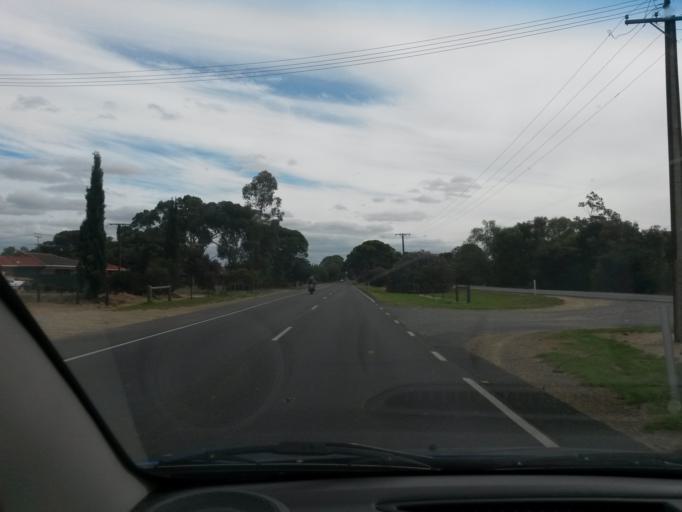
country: AU
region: South Australia
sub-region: Salisbury
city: Salisbury
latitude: -34.7787
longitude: 138.6584
